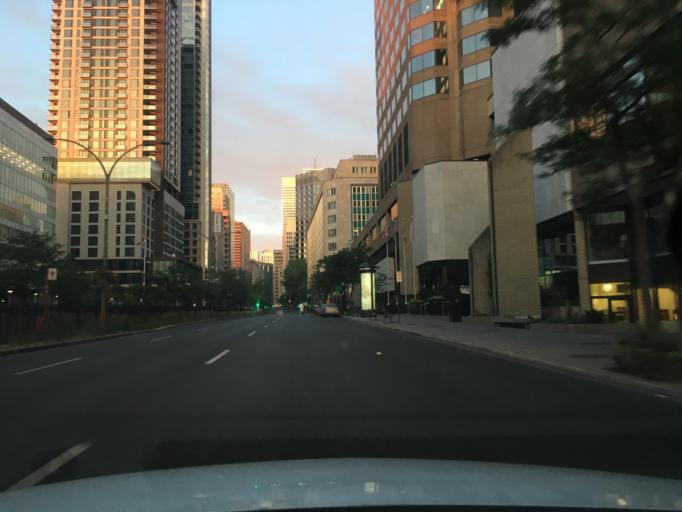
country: CA
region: Quebec
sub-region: Montreal
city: Montreal
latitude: 45.5075
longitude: -73.5630
